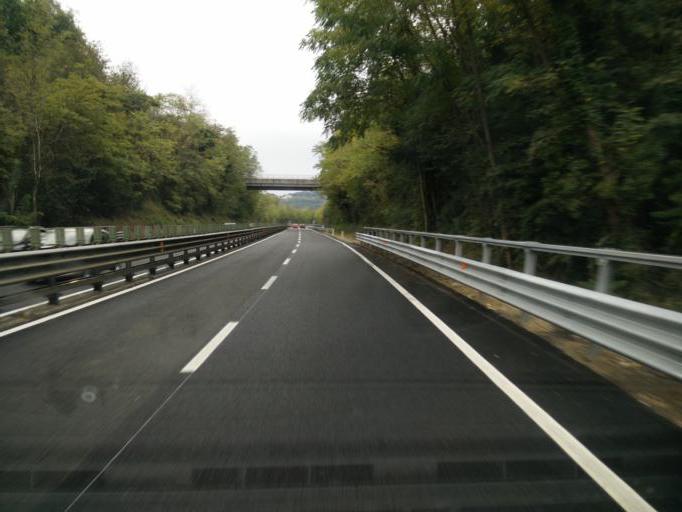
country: IT
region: Tuscany
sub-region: Provincia di Siena
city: Bellavista
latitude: 43.4495
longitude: 11.1535
